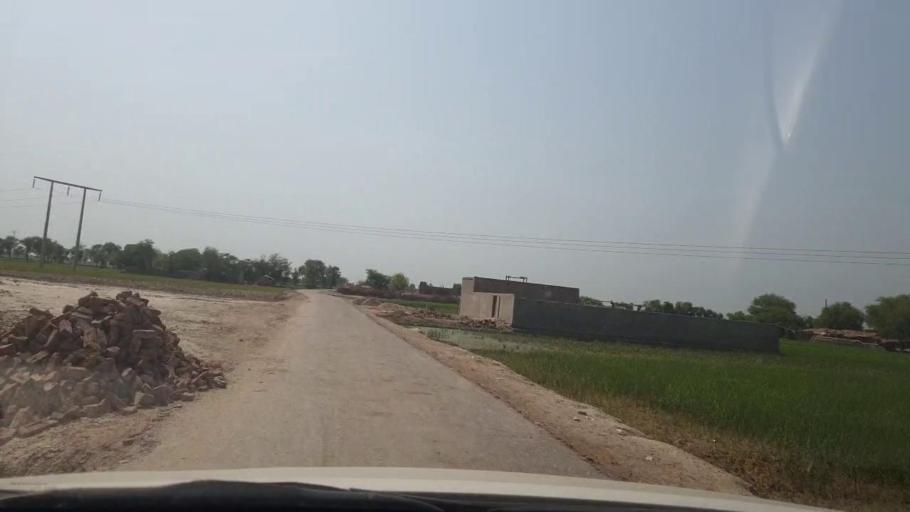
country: PK
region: Sindh
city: Rustam jo Goth
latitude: 28.0033
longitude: 68.7187
